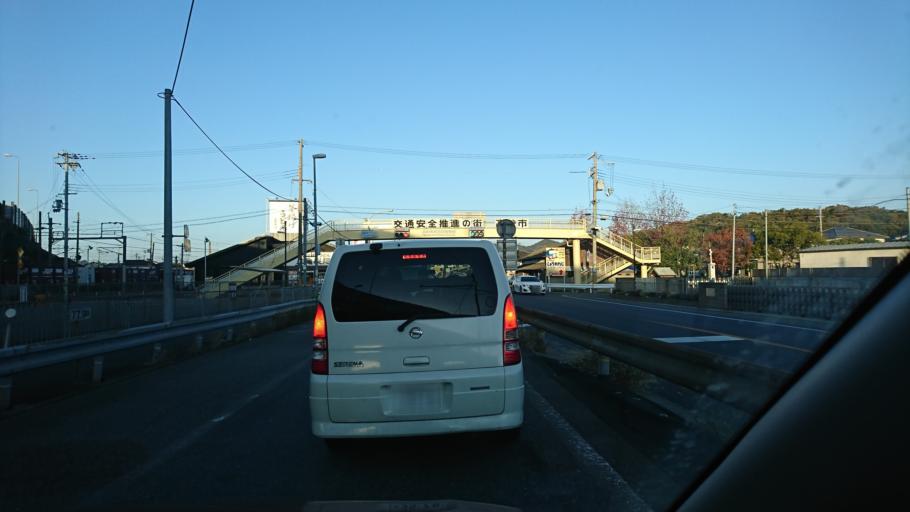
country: JP
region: Hyogo
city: Kakogawacho-honmachi
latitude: 34.7909
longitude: 134.7972
